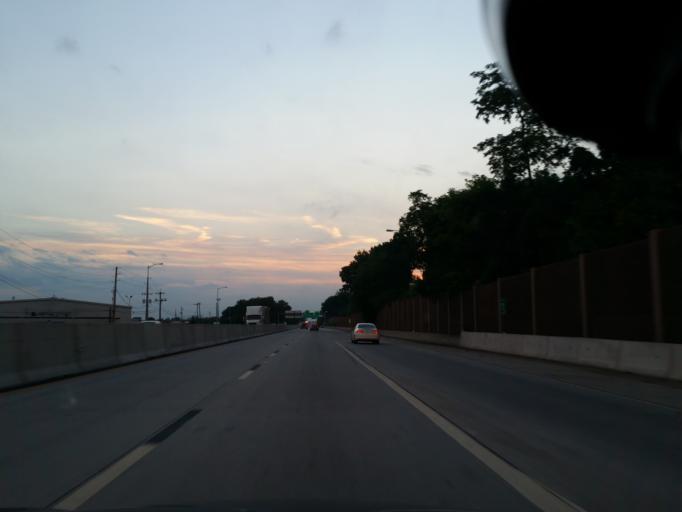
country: US
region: Pennsylvania
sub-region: Cumberland County
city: Camp Hill
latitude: 40.2319
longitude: -76.9365
